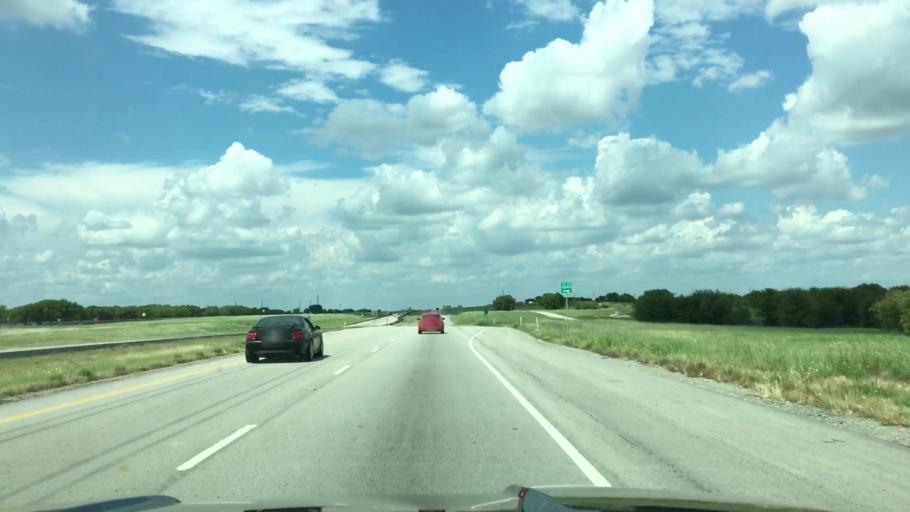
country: US
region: Texas
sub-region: Wise County
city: Newark
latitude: 33.0098
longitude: -97.4376
